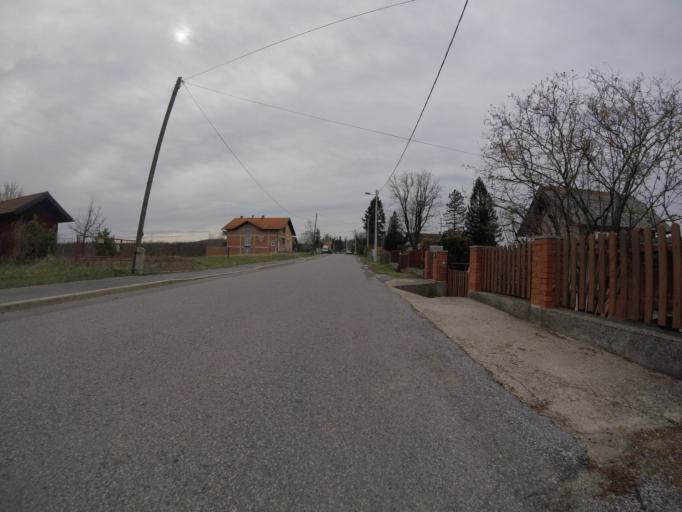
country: HR
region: Grad Zagreb
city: Strmec
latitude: 45.6421
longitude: 15.9354
